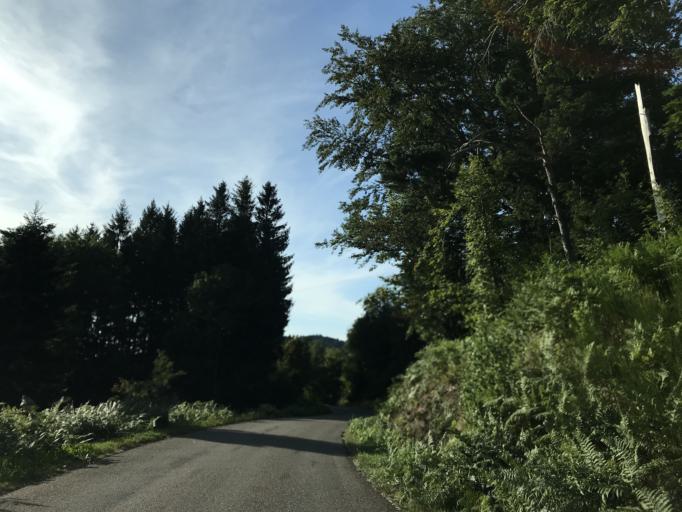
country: FR
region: Auvergne
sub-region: Departement du Puy-de-Dome
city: Job
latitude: 45.6747
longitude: 3.7354
